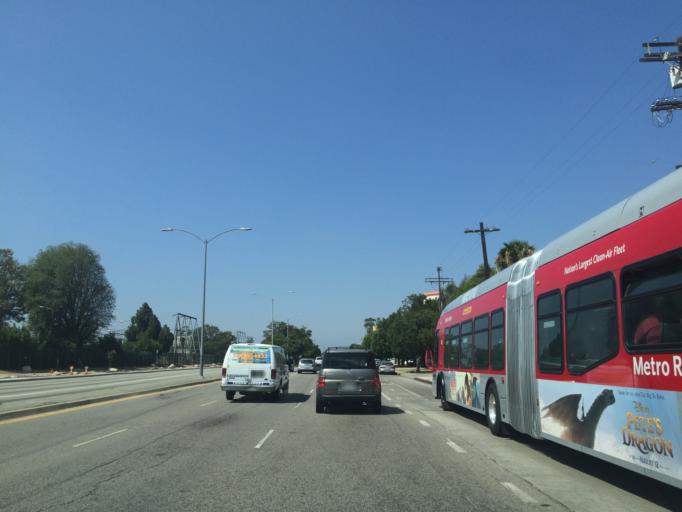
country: US
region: California
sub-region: Los Angeles County
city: Culver City
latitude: 34.0399
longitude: -118.3700
